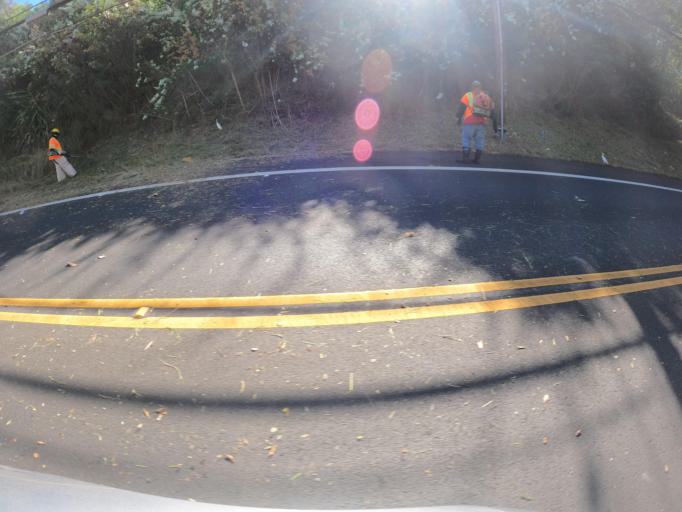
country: US
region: Hawaii
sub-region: Honolulu County
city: Halawa Heights
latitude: 21.3817
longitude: -157.9144
